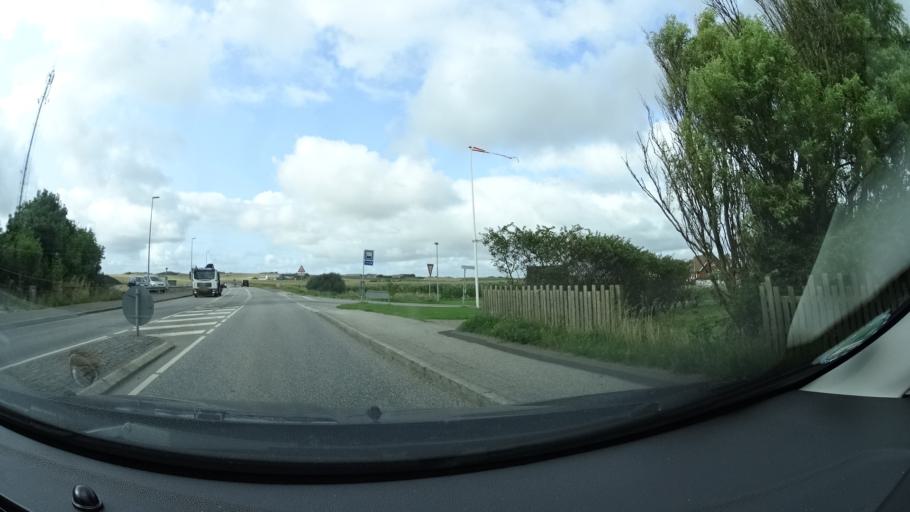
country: DK
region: Central Jutland
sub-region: Lemvig Kommune
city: Harboore
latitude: 56.5676
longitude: 8.2196
